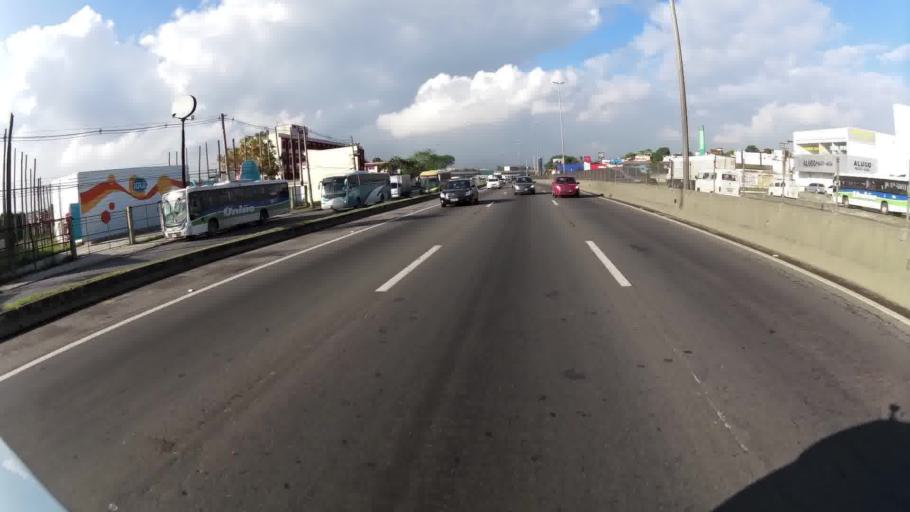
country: BR
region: Rio de Janeiro
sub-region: Duque De Caxias
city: Duque de Caxias
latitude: -22.7976
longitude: -43.2894
